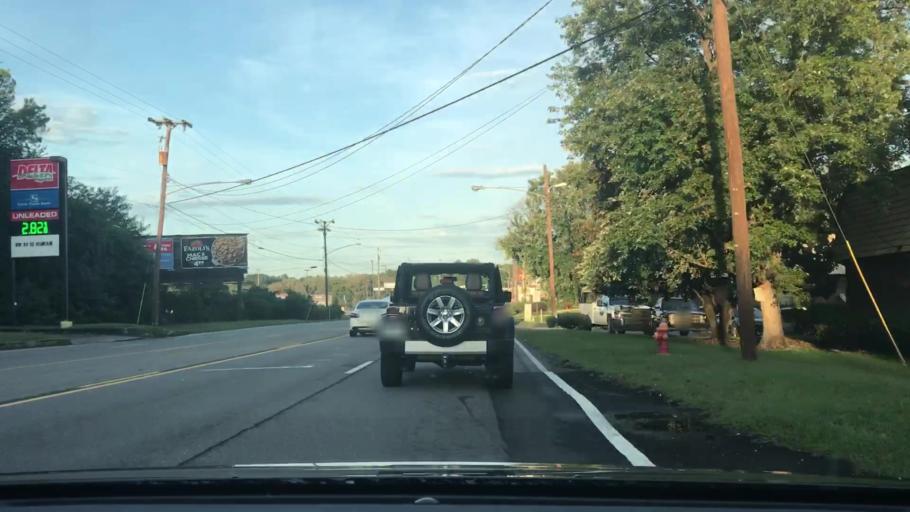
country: US
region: Tennessee
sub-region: Davidson County
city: Oak Hill
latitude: 36.0783
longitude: -86.7298
